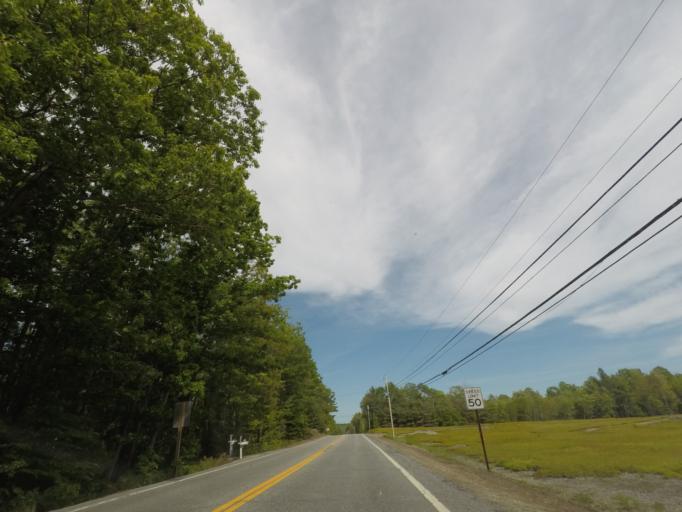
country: US
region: Maine
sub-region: Sagadahoc County
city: Richmond
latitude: 44.0874
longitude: -69.7696
